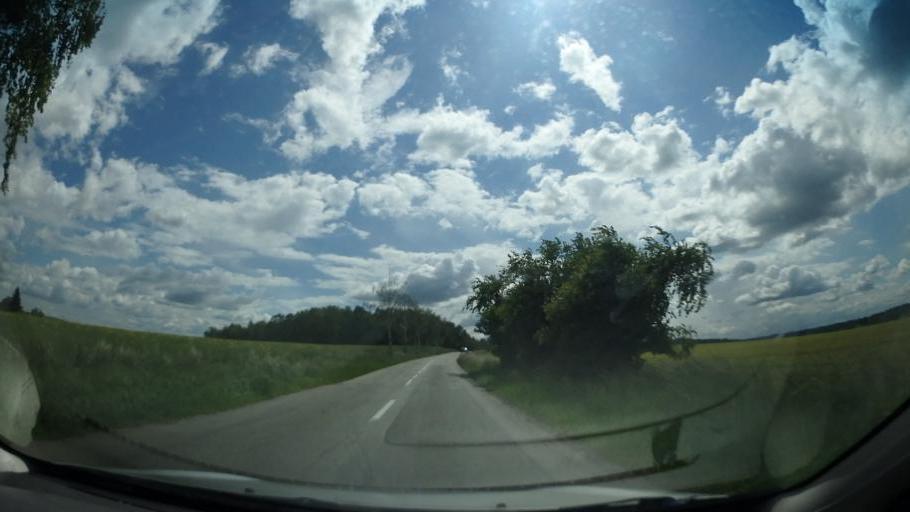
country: CZ
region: South Moravian
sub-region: Okres Blansko
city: Letovice
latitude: 49.5877
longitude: 16.5949
